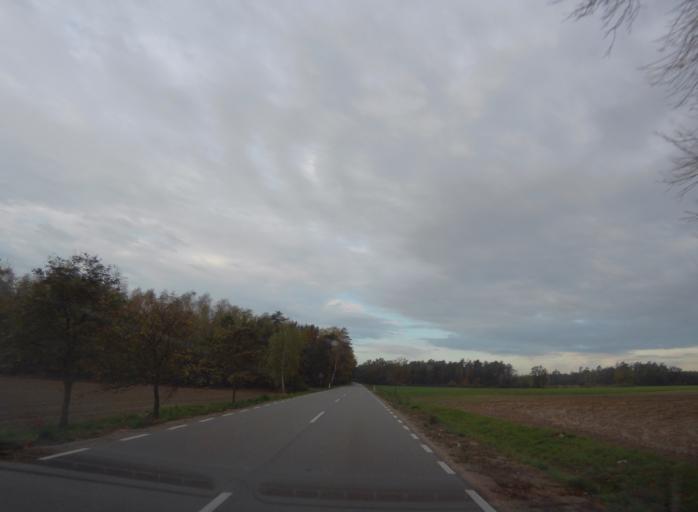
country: PL
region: Masovian Voivodeship
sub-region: Powiat losicki
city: Stara Kornica
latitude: 52.1825
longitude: 22.8520
